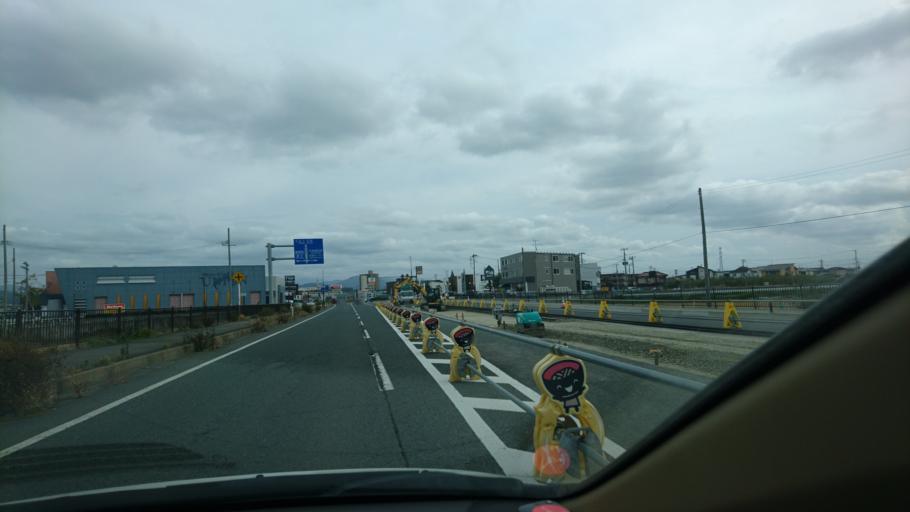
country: JP
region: Iwate
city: Morioka-shi
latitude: 39.6872
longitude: 141.1171
